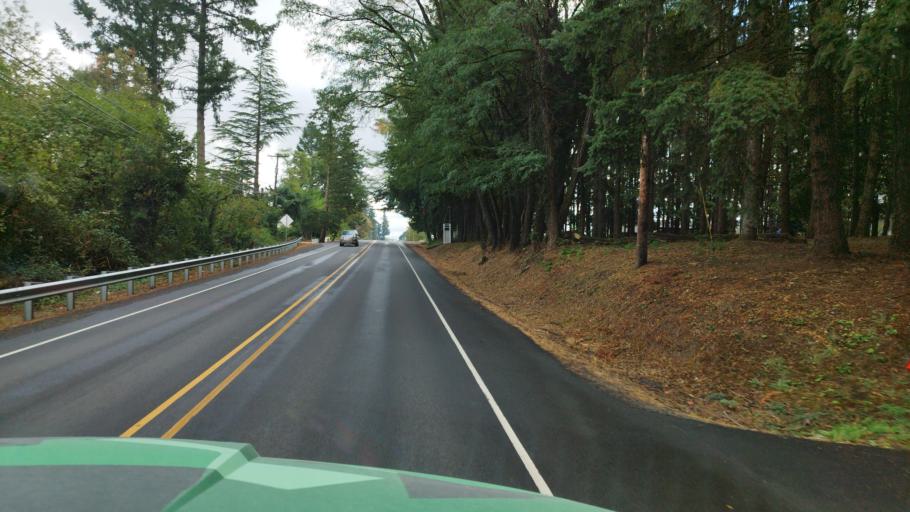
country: US
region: Oregon
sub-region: Yamhill County
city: Lafayette
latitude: 45.2428
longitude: -123.1083
